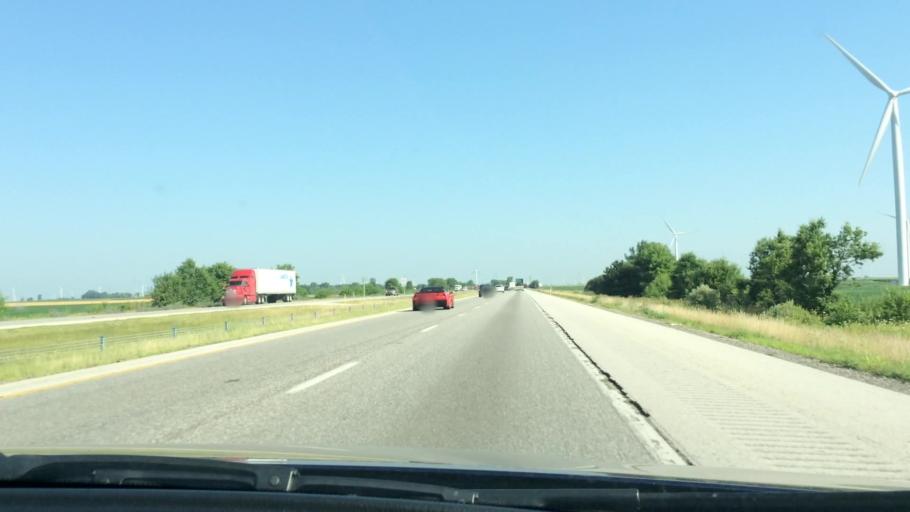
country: US
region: Indiana
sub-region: White County
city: Brookston
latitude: 40.5704
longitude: -86.9429
